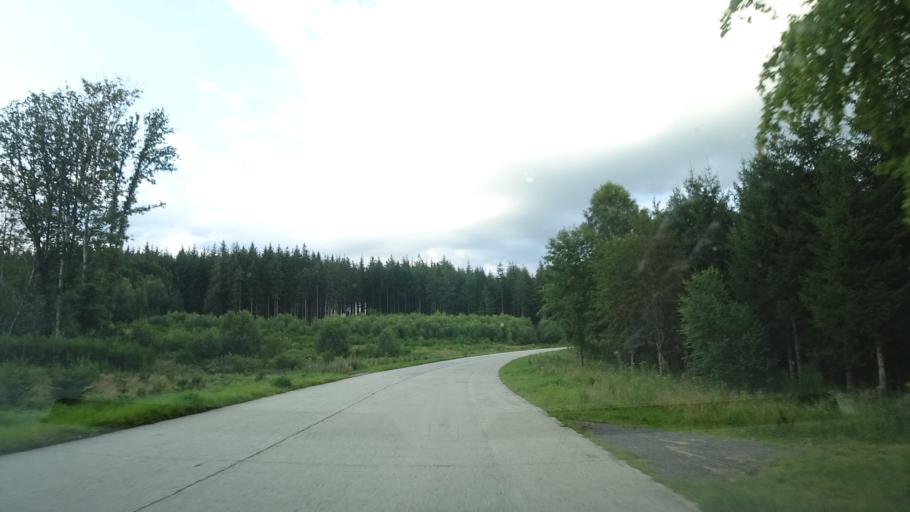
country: BE
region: Wallonia
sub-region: Province du Luxembourg
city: Herbeumont
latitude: 49.7909
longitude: 5.2537
